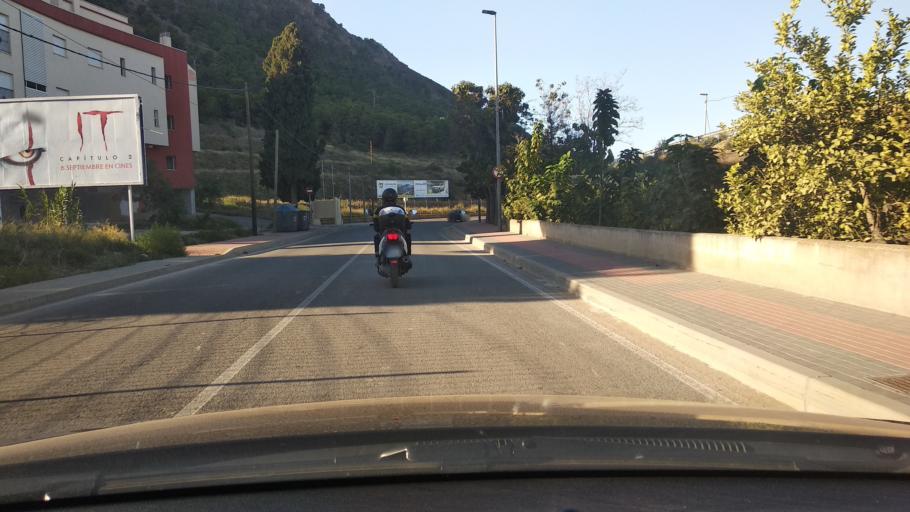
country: ES
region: Murcia
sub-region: Murcia
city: Beniel
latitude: 37.9884
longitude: -1.0422
